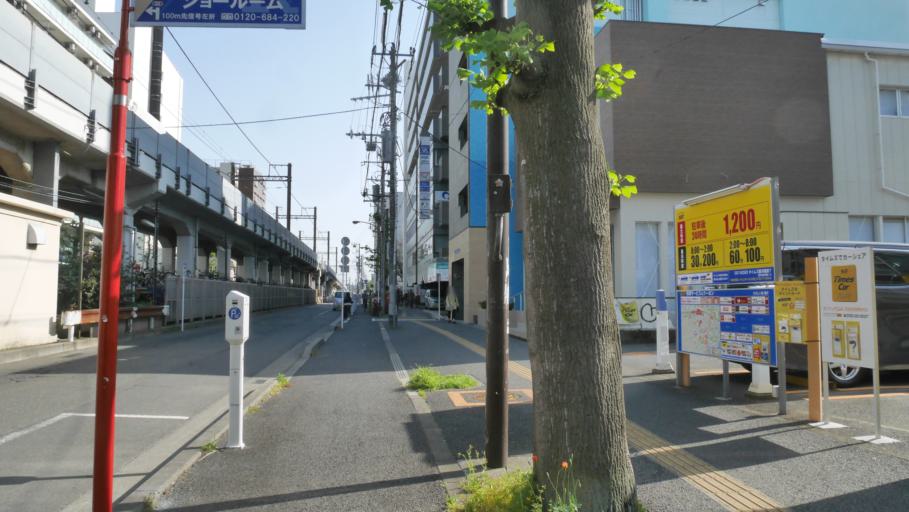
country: JP
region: Kanagawa
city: Fujisawa
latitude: 35.3359
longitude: 139.4863
